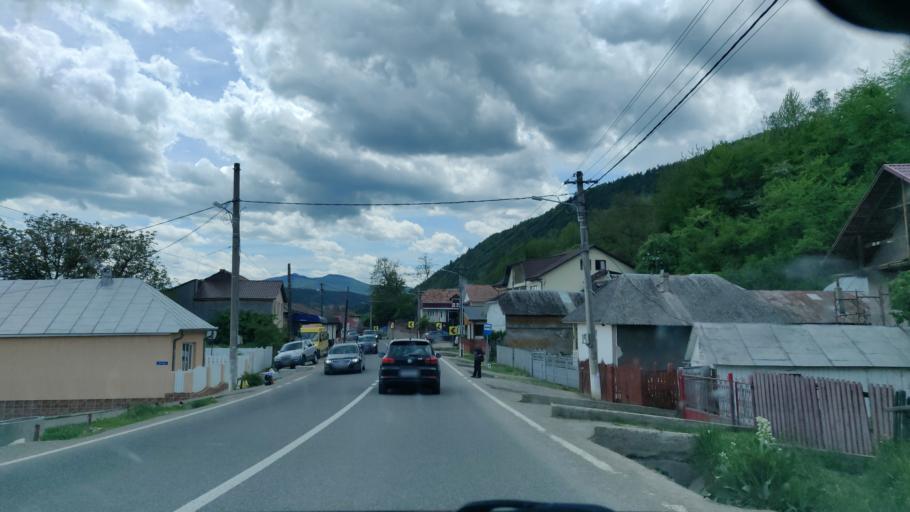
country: RO
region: Vrancea
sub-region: Comuna Tulnici
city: Tulnici
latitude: 45.9190
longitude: 26.6731
